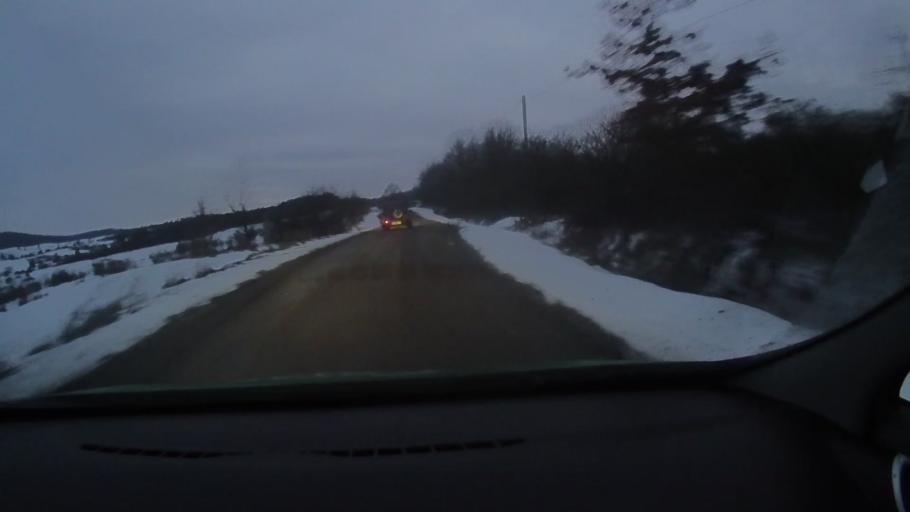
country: RO
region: Harghita
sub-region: Comuna Darjiu
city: Darjiu
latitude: 46.1894
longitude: 25.2472
